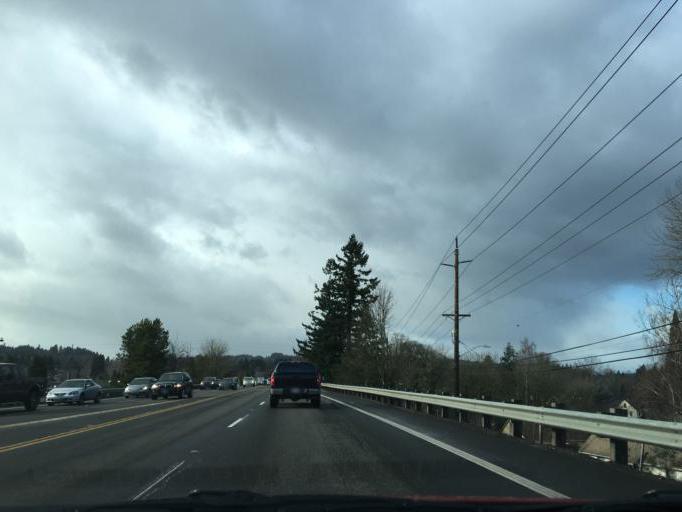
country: US
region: Oregon
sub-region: Washington County
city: Tigard
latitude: 45.4325
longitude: -122.7692
